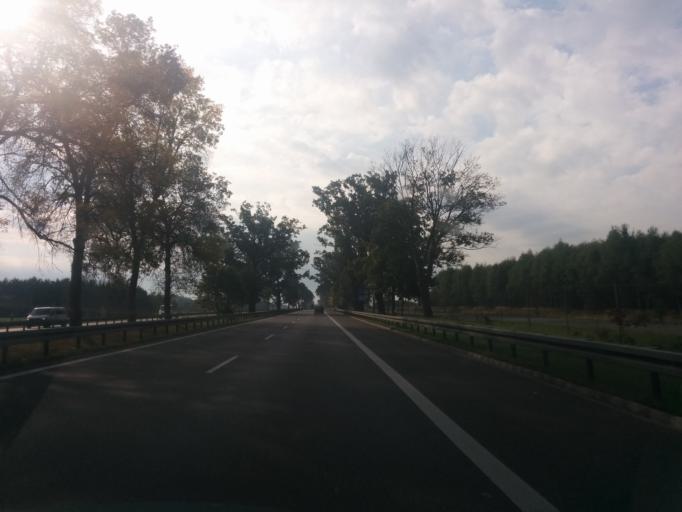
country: PL
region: Masovian Voivodeship
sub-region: Powiat bialobrzeski
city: Sucha
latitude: 51.5967
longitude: 20.9910
